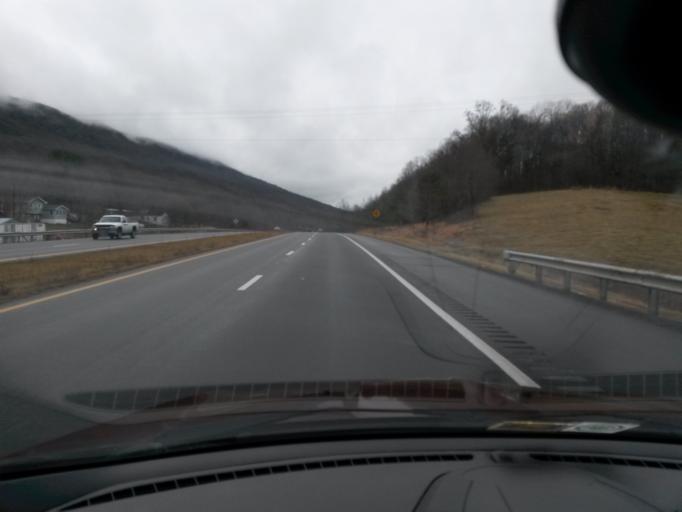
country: US
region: West Virginia
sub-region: Mercer County
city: Bluefield
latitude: 37.2803
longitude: -81.1383
